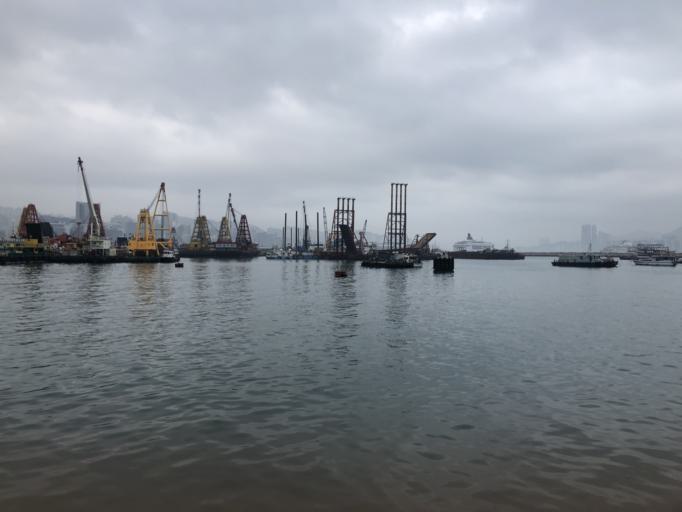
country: HK
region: Kowloon City
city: Kowloon
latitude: 22.3152
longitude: 114.1940
